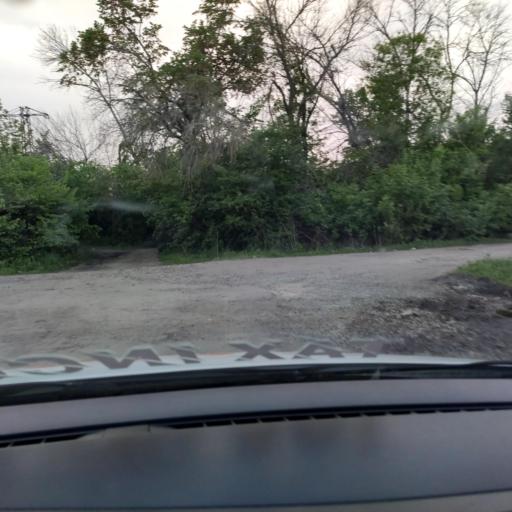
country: RU
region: Voronezj
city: Maslovka
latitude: 51.4485
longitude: 39.2343
